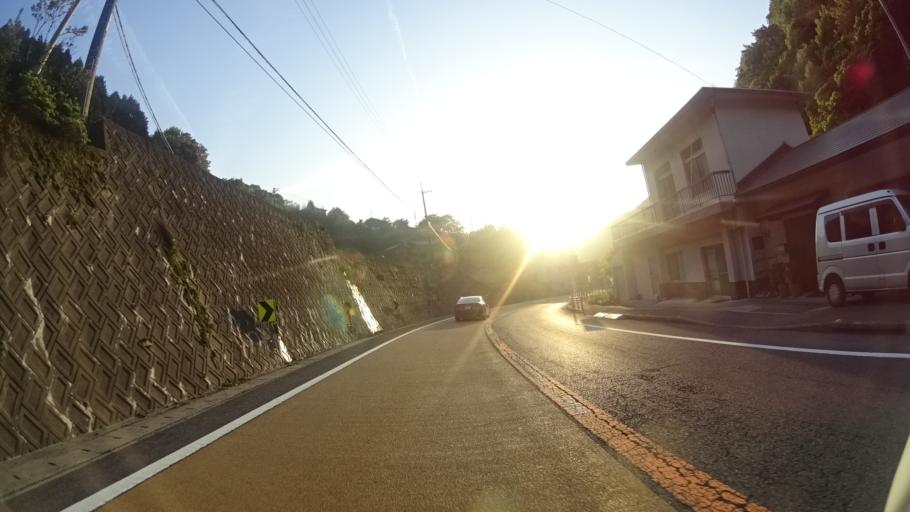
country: JP
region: Ehime
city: Kawanoecho
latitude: 33.9957
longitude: 133.6651
